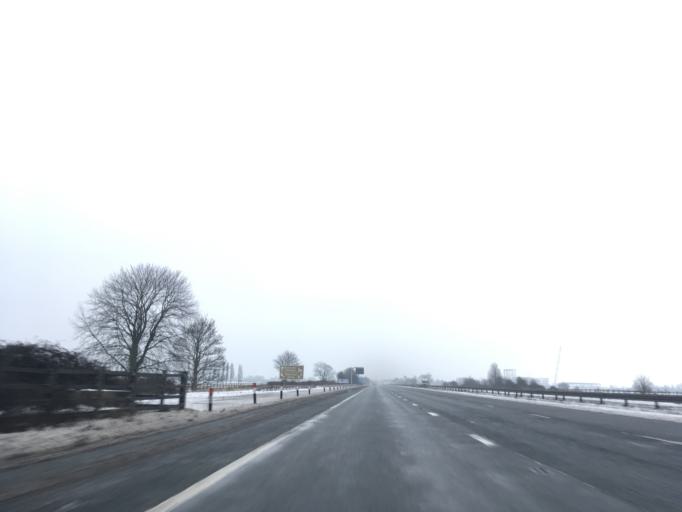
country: GB
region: England
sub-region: Gloucestershire
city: Stonehouse
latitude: 51.7850
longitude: -2.3027
